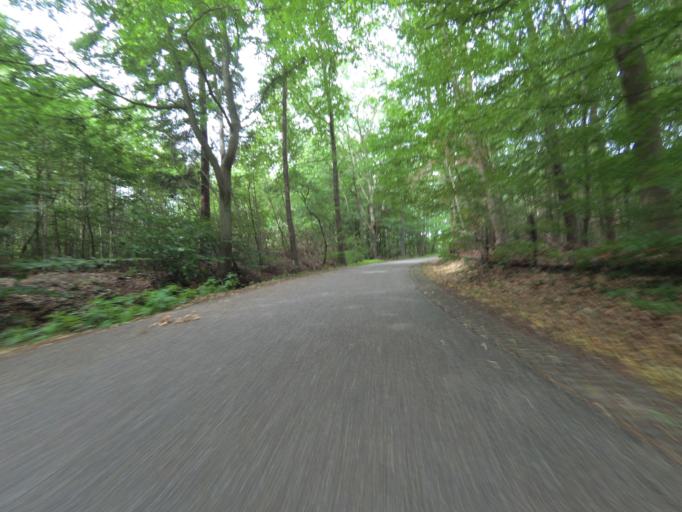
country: NL
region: Overijssel
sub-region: Gemeente Enschede
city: Enschede
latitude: 52.2360
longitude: 6.9281
